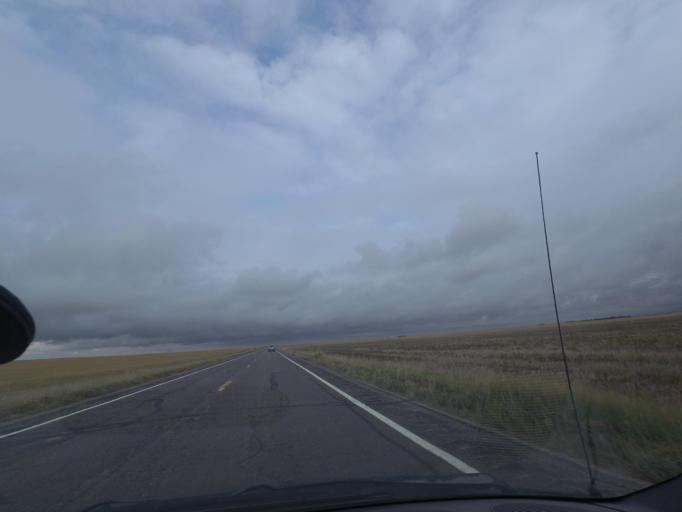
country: US
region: Colorado
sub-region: Washington County
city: Akron
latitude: 39.6991
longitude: -103.0079
